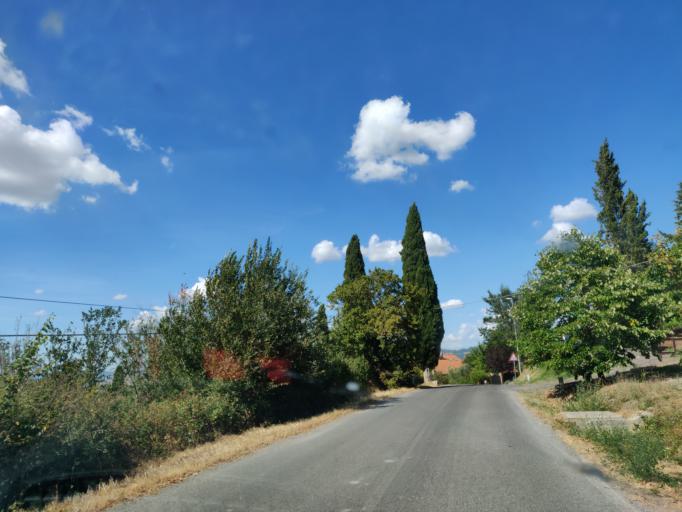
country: IT
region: Tuscany
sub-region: Provincia di Siena
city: Radicofani
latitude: 42.9730
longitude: 11.7373
